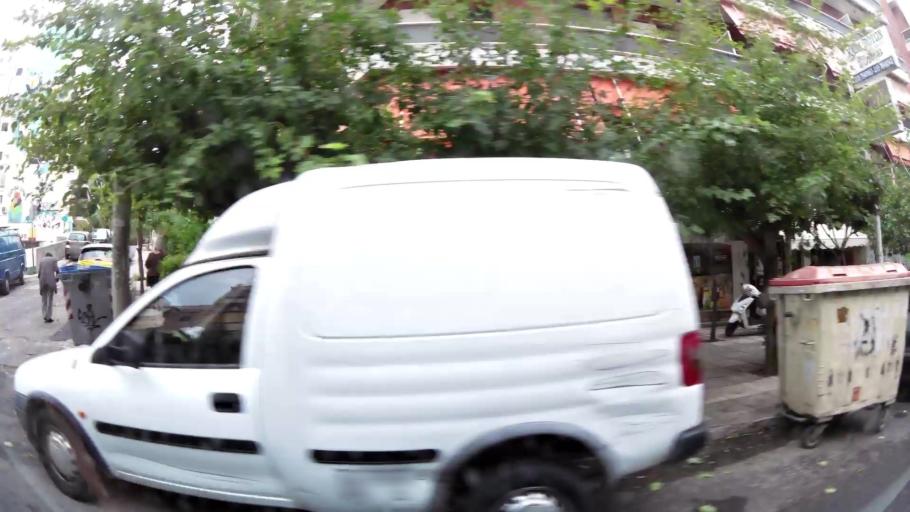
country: GR
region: Attica
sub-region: Nomarchia Athinas
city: Vyronas
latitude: 37.9632
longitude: 23.7581
